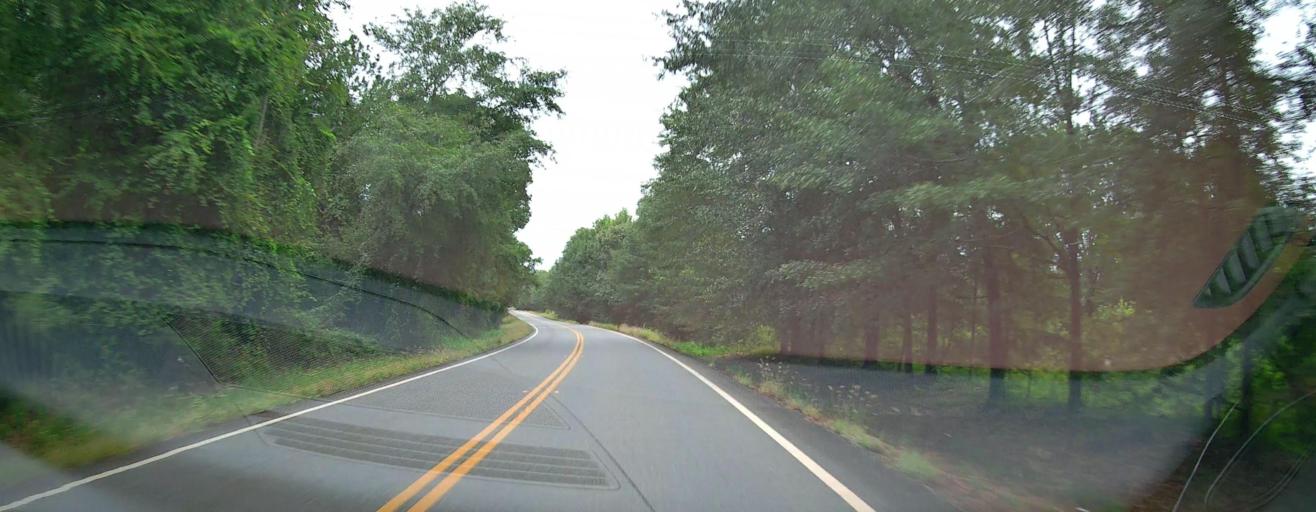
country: US
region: Georgia
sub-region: Marion County
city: Buena Vista
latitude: 32.2769
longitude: -84.4355
